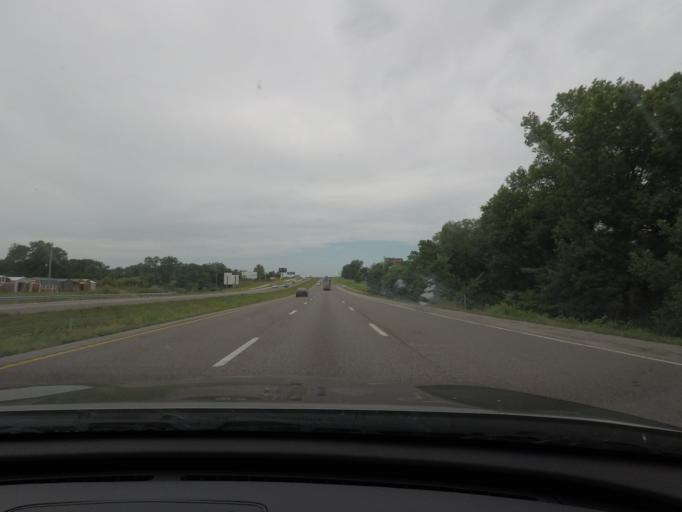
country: US
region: Missouri
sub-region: Boone County
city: Hallsville
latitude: 38.9538
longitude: -92.1318
